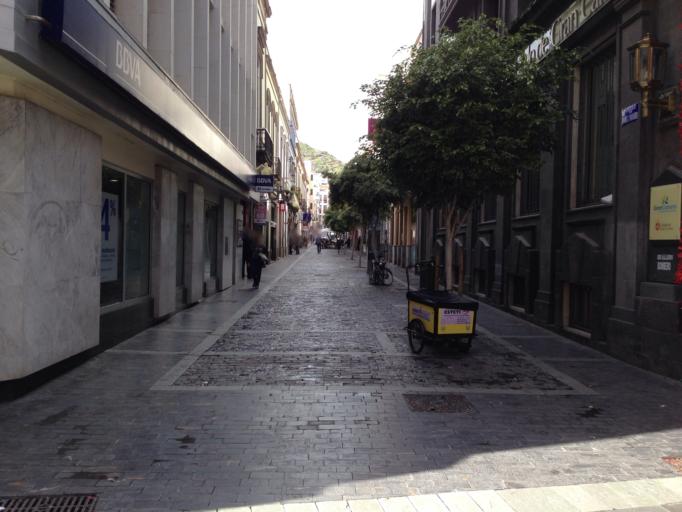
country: ES
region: Canary Islands
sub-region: Provincia de Las Palmas
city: Las Palmas de Gran Canaria
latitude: 28.1073
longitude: -15.4169
